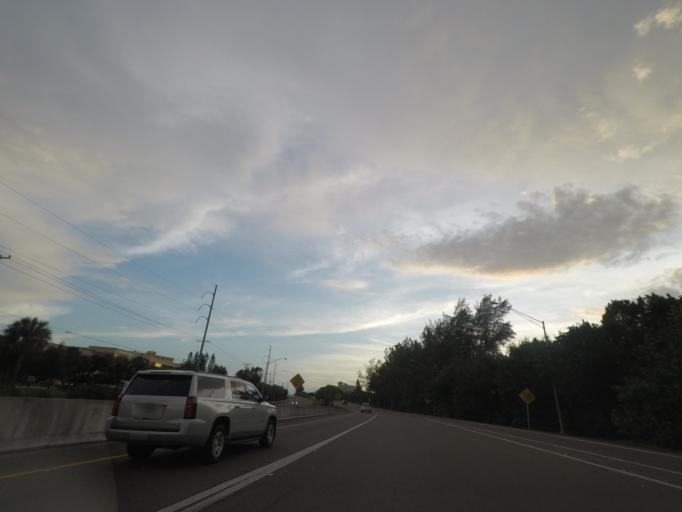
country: US
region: Florida
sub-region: Pinellas County
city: Gulfport
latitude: 27.7191
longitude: -82.6944
